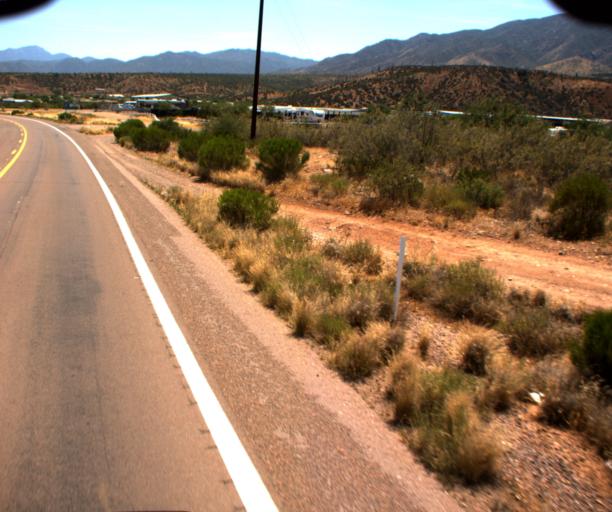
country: US
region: Arizona
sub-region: Gila County
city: Tonto Basin
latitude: 33.8525
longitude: -111.3107
